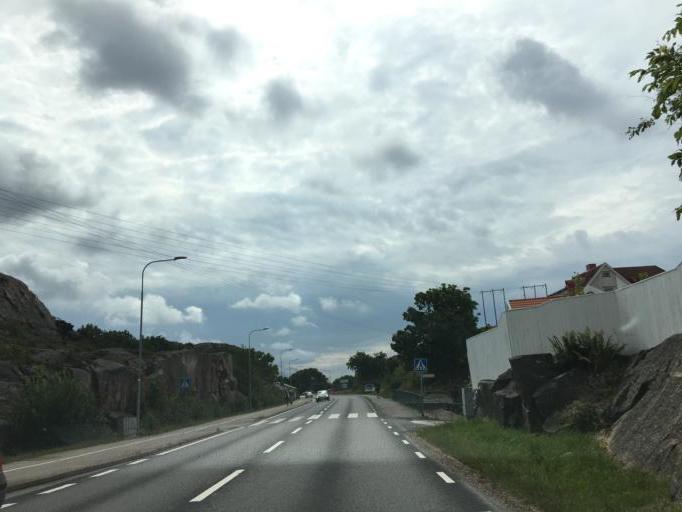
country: SE
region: Vaestra Goetaland
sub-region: Sotenas Kommun
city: Kungshamn
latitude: 58.3700
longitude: 11.2505
